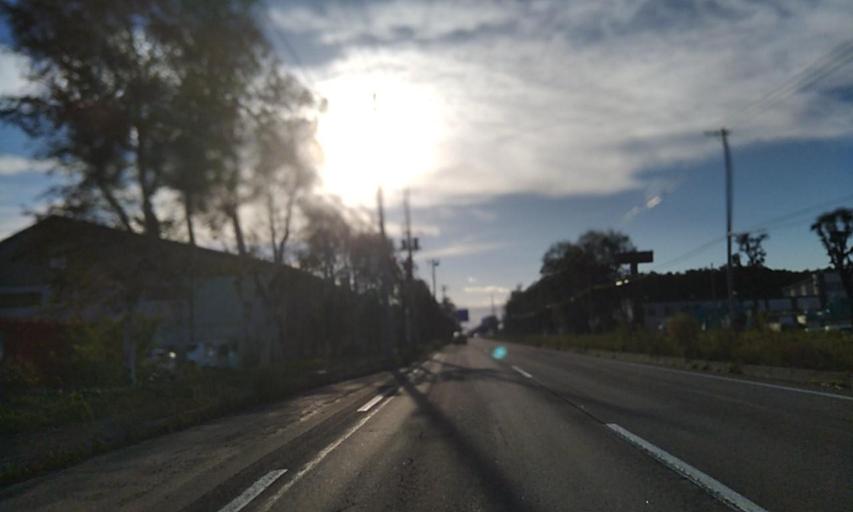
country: JP
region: Hokkaido
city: Obihiro
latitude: 42.9277
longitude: 143.1460
